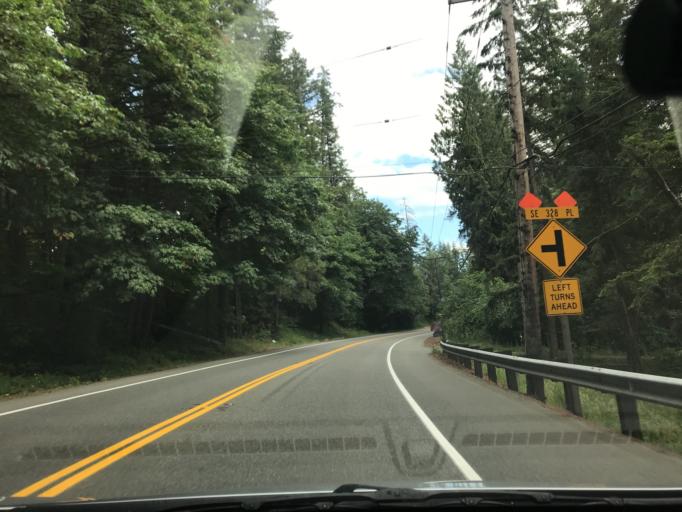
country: US
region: Washington
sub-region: King County
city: Lake Morton-Berrydale
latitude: 47.3075
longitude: -122.0881
